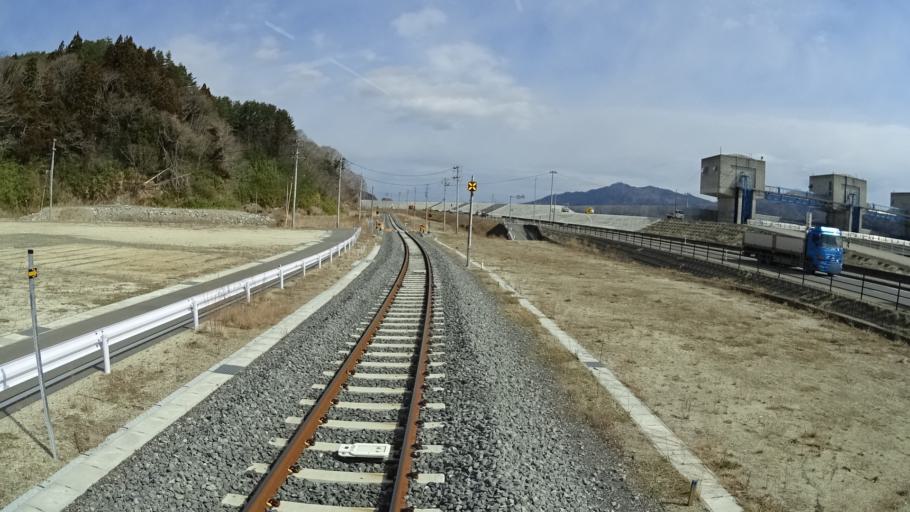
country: JP
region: Iwate
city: Miyako
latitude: 39.5853
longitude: 141.9438
